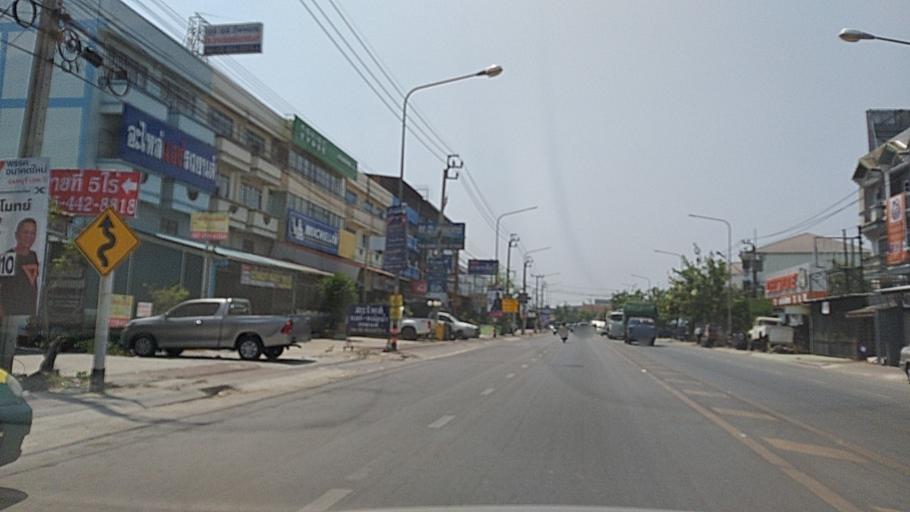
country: TH
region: Nonthaburi
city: Bang Bua Thong
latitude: 13.9094
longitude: 100.3904
